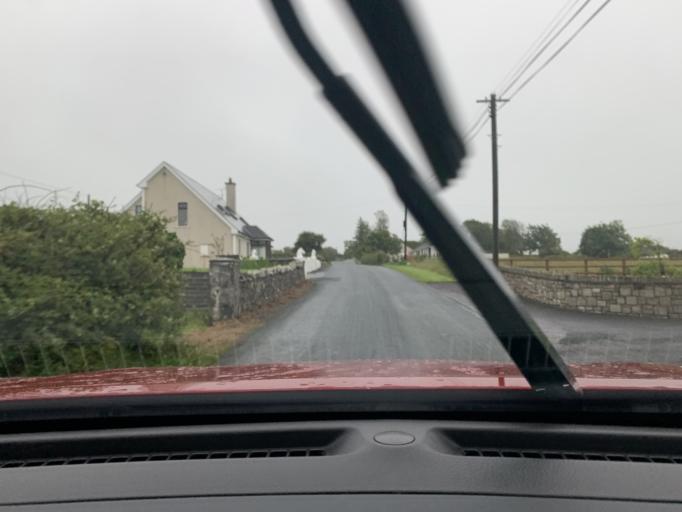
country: IE
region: Connaught
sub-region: County Leitrim
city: Kinlough
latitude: 54.4414
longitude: -8.4386
